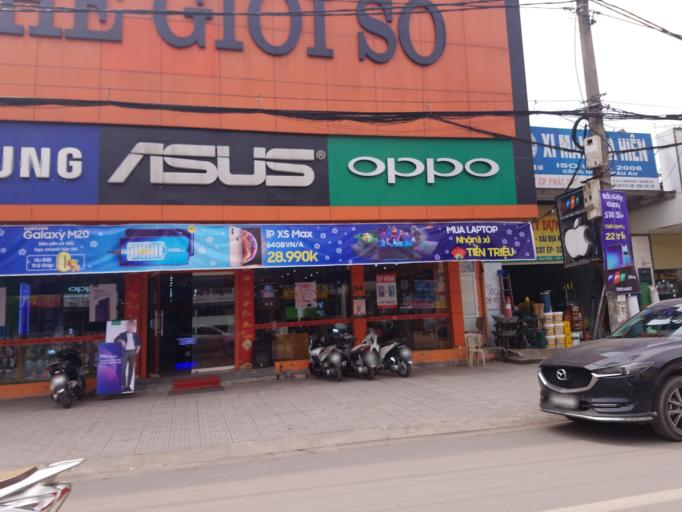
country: VN
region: Thai Nguyen
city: Thanh Pho Thai Nguyen
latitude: 21.5970
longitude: 105.8243
